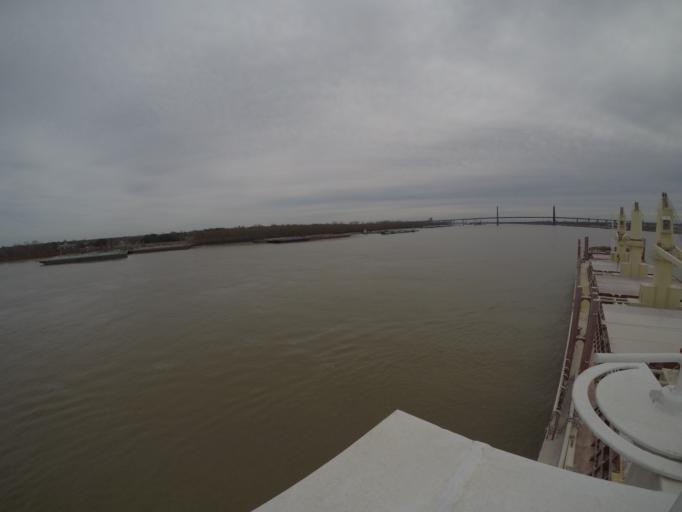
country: US
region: Louisiana
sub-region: Saint Charles Parish
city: New Sarpy
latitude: 29.9514
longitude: -90.3925
